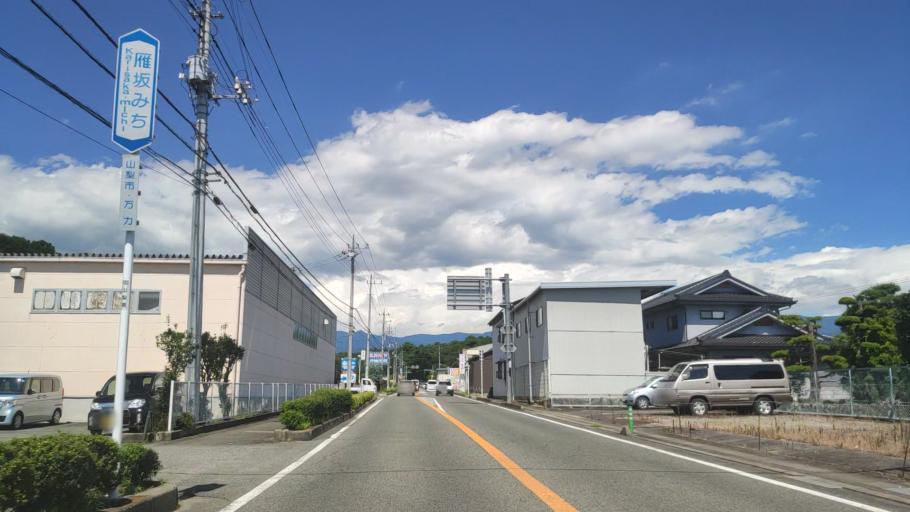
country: JP
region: Yamanashi
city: Enzan
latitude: 35.6887
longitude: 138.6766
